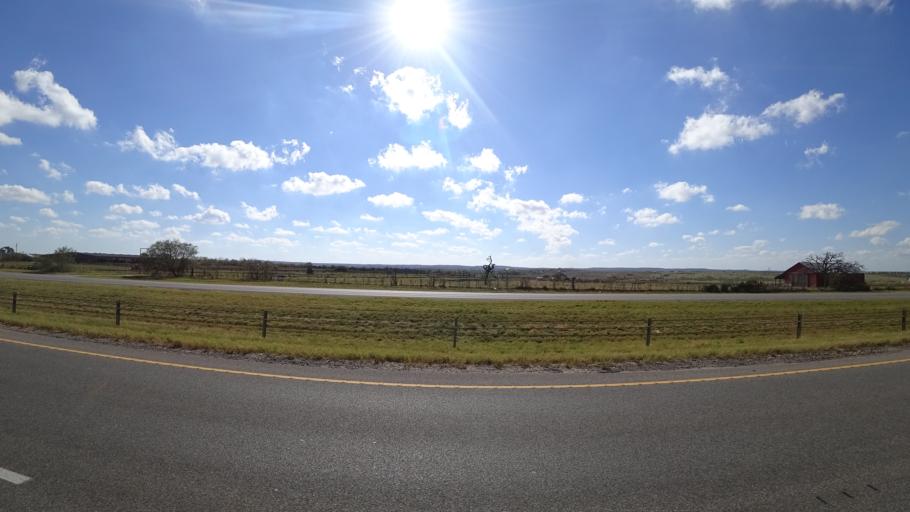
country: US
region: Texas
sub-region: Travis County
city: Garfield
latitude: 30.1889
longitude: -97.5873
